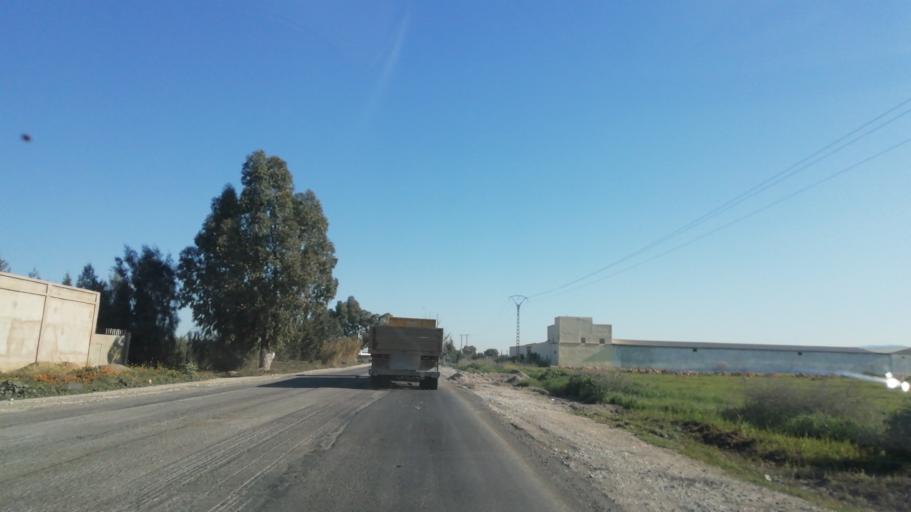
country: DZ
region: Relizane
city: Zemoura
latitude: 35.7553
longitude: 0.6777
